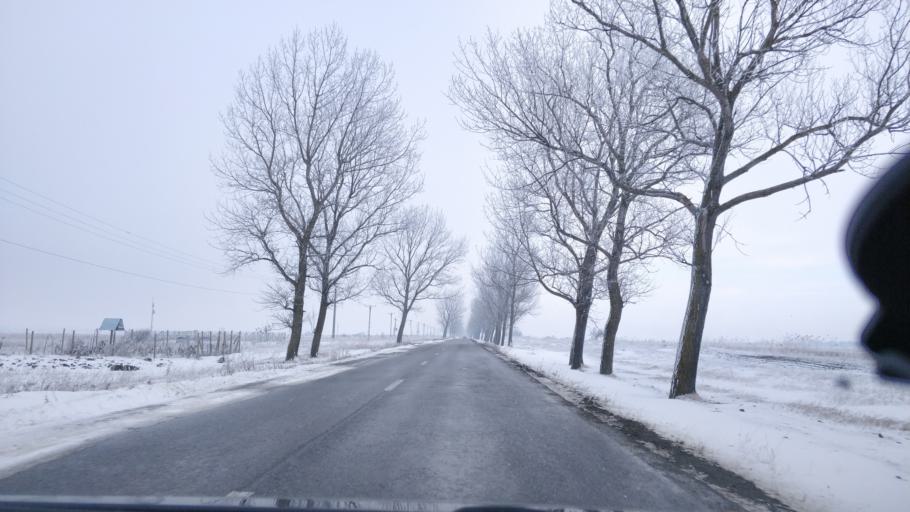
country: RO
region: Vrancea
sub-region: Comuna Vanatori
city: Jorasti
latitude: 45.6976
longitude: 27.2404
